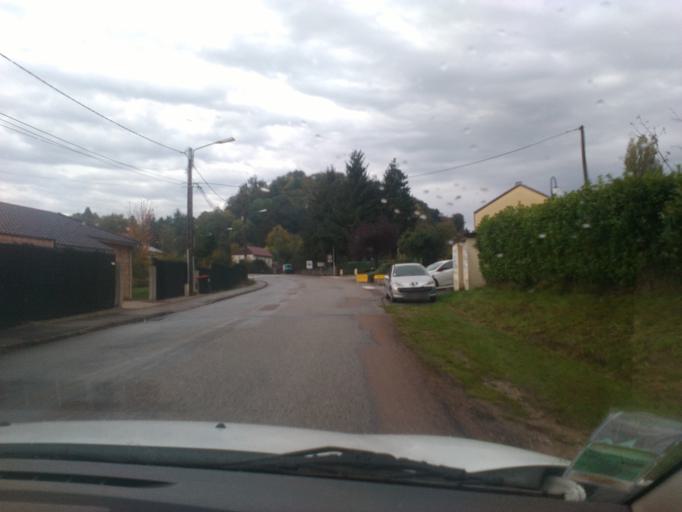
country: FR
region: Lorraine
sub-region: Departement des Vosges
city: Bruyeres
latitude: 48.2168
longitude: 6.7225
